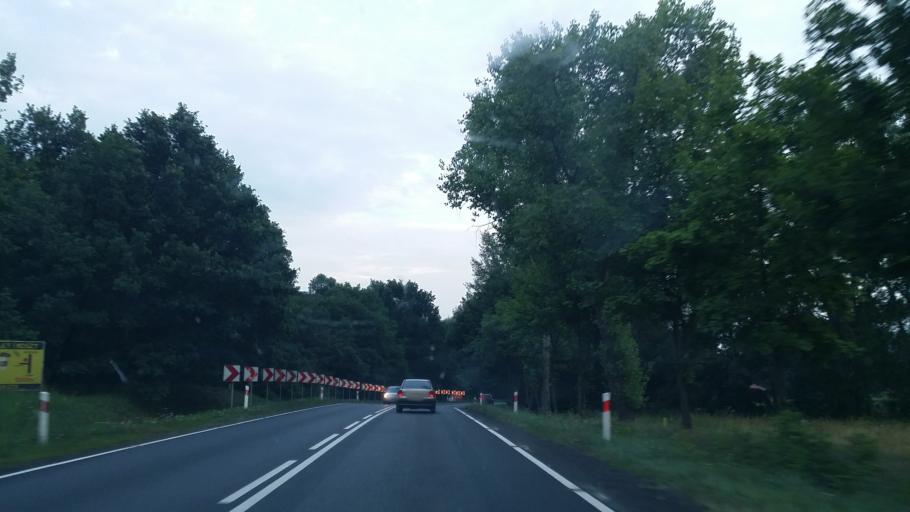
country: PL
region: Lower Silesian Voivodeship
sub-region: Powiat lubinski
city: Osiek
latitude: 51.3756
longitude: 16.2345
